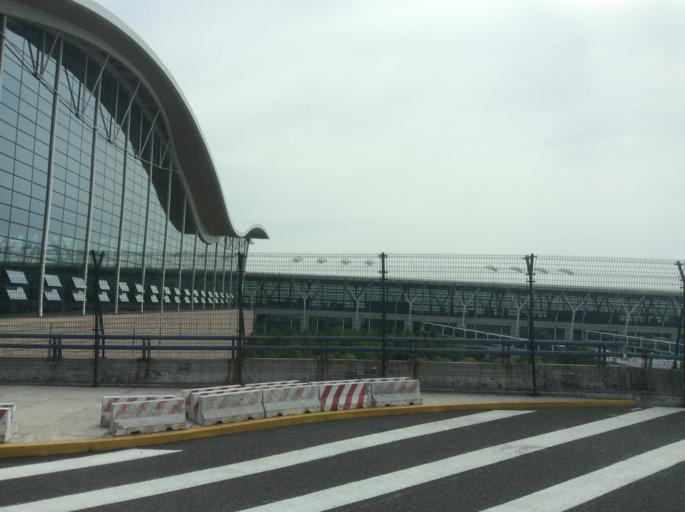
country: CN
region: Shanghai Shi
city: Laogang
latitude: 31.1512
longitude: 121.8046
